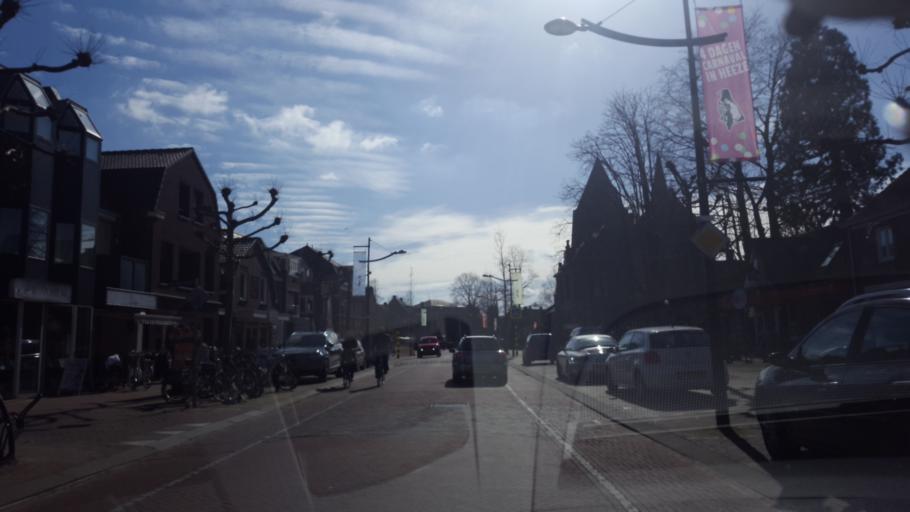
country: NL
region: North Brabant
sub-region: Gemeente Heeze-Leende
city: Heeze
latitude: 51.3790
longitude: 5.5779
